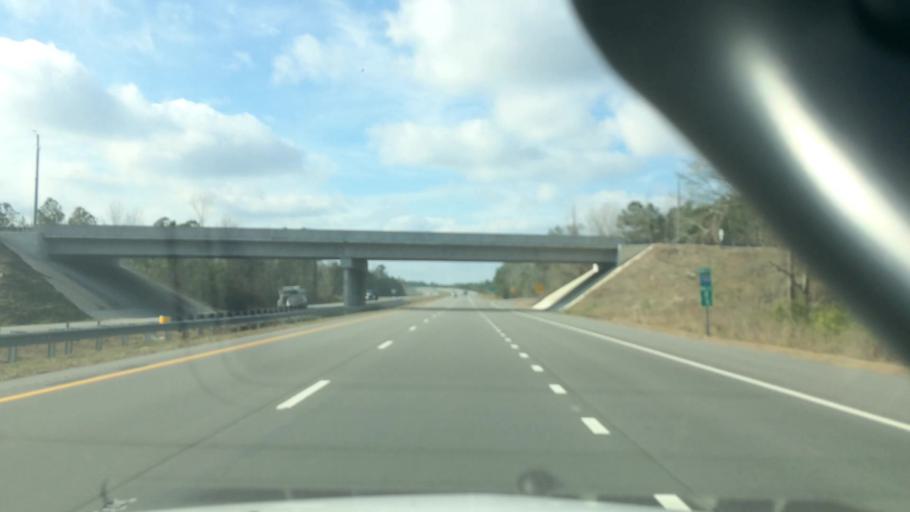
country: US
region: North Carolina
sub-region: Brunswick County
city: Leland
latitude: 34.2776
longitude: -78.0482
